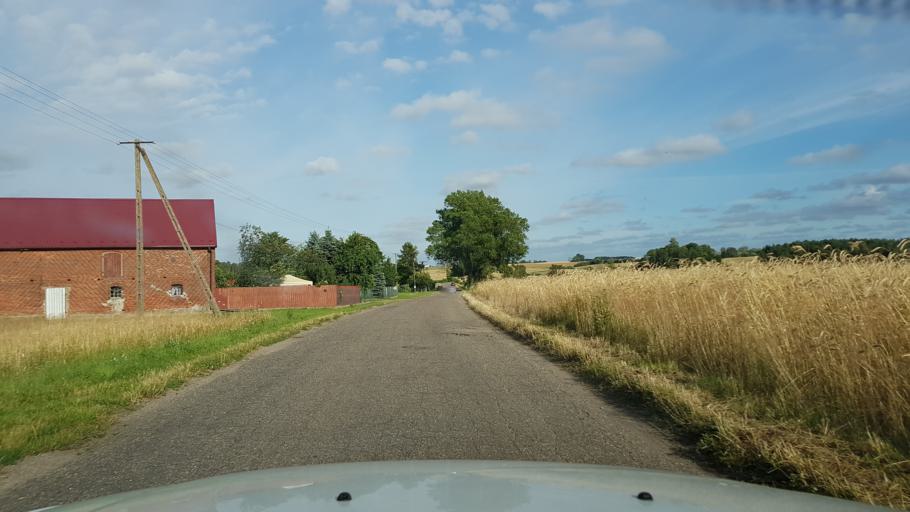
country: PL
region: West Pomeranian Voivodeship
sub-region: Powiat kolobrzeski
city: Grzybowo
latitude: 54.0911
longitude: 15.5468
